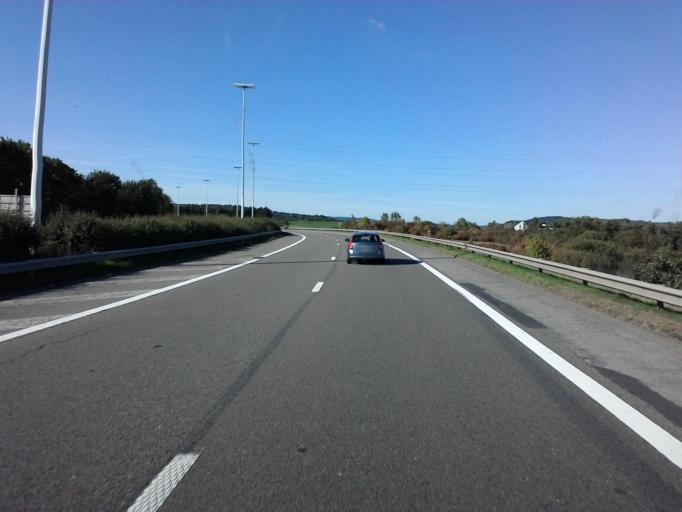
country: BE
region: Wallonia
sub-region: Province du Luxembourg
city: Aubange
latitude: 49.5718
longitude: 5.8217
